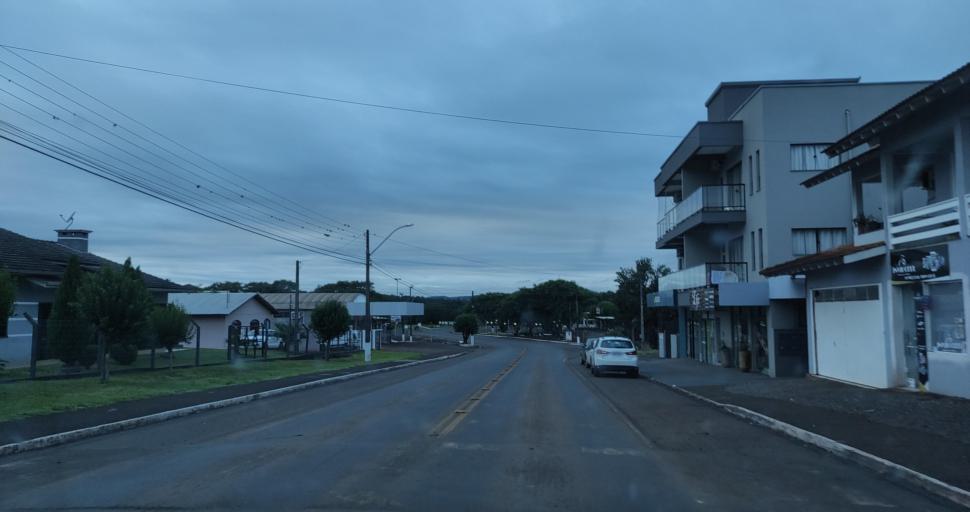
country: BR
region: Santa Catarina
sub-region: Xanxere
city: Xanxere
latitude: -26.7336
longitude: -52.3919
